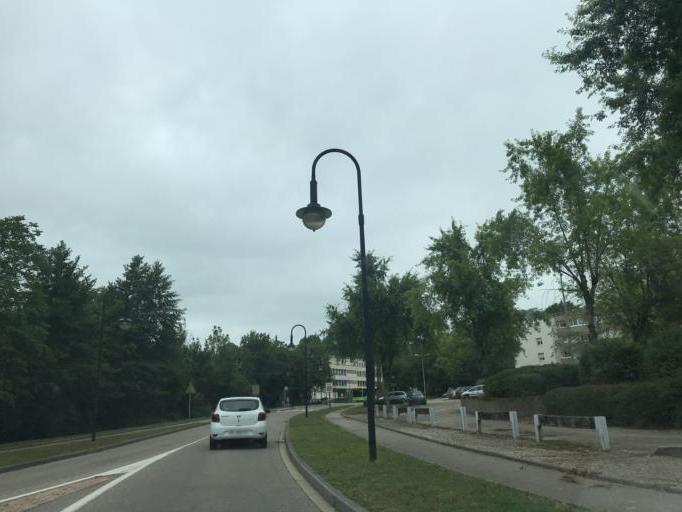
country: FR
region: Rhone-Alpes
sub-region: Departement de l'Ain
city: Arbent
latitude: 46.2919
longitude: 5.6772
